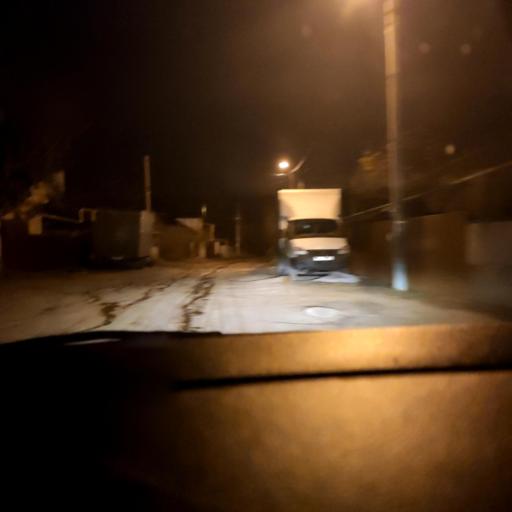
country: RU
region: Voronezj
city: Podgornoye
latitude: 51.7306
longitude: 39.1469
